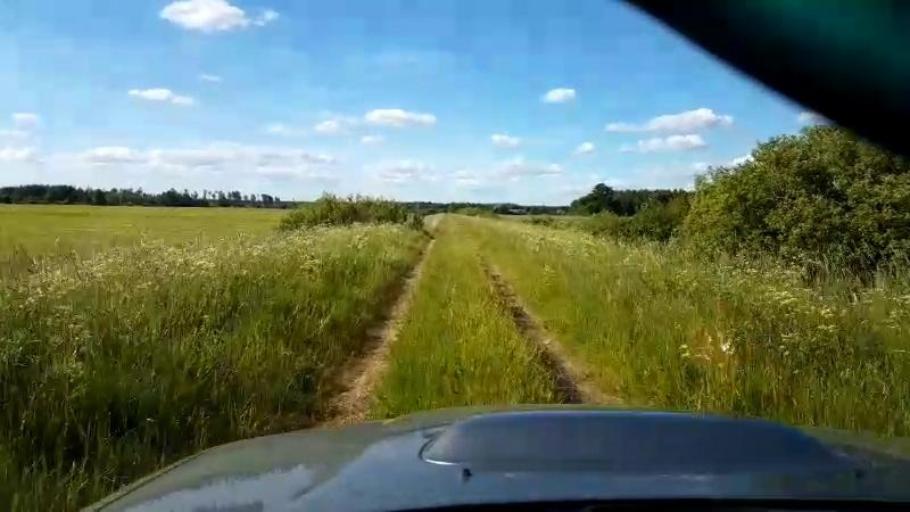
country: EE
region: Paernumaa
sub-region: Sauga vald
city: Sauga
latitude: 58.4967
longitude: 24.5914
